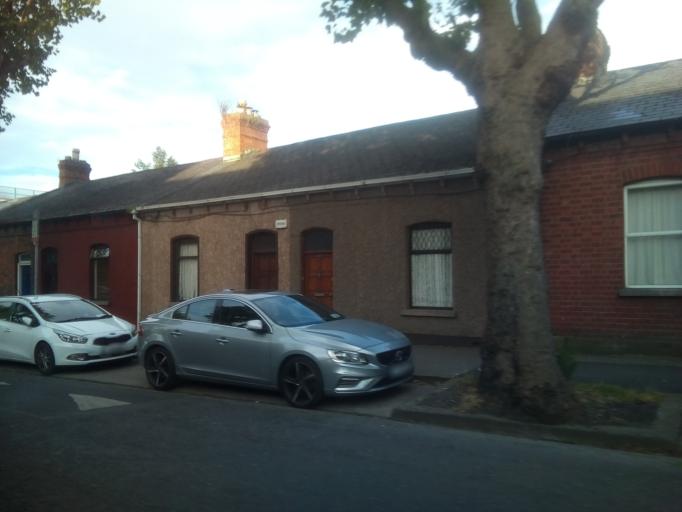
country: IE
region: Leinster
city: Crumlin
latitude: 53.3362
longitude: -6.3236
